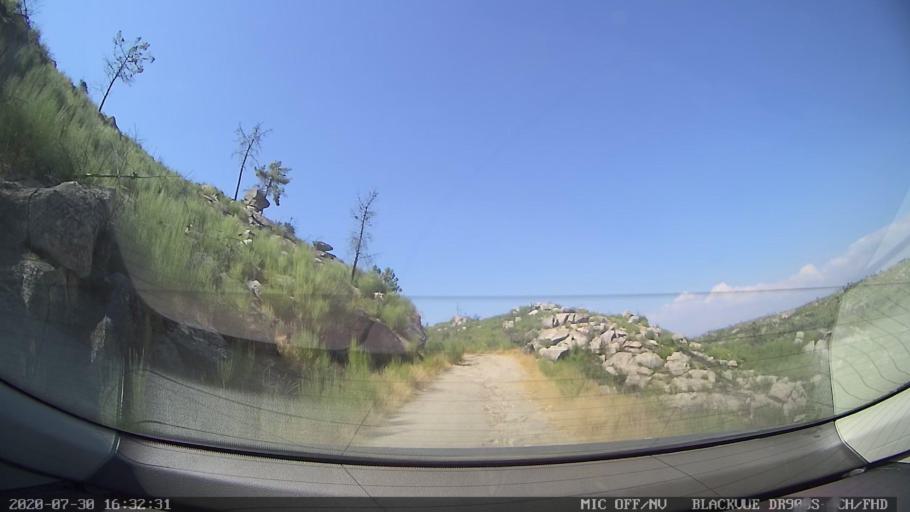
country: PT
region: Vila Real
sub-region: Sabrosa
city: Sabrosa
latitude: 41.3114
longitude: -7.4918
